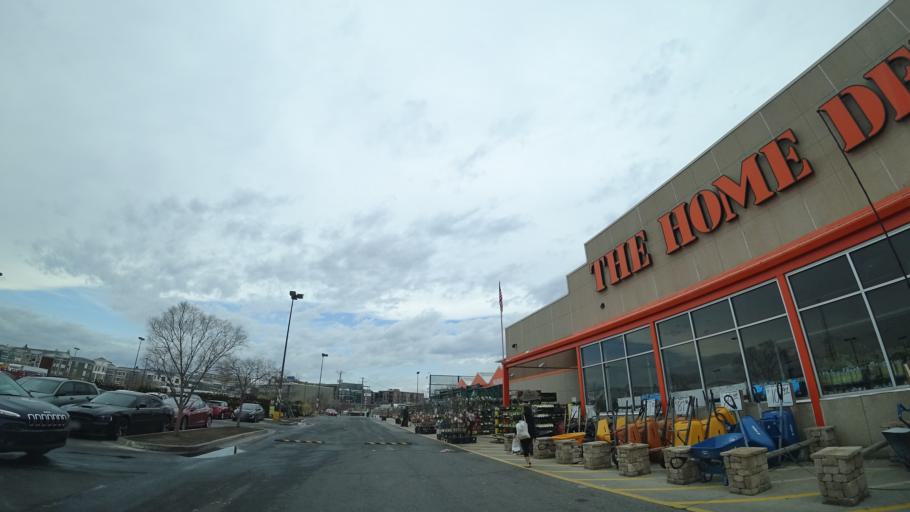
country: US
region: Maryland
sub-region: Prince George's County
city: Mount Rainier
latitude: 38.9206
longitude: -76.9915
